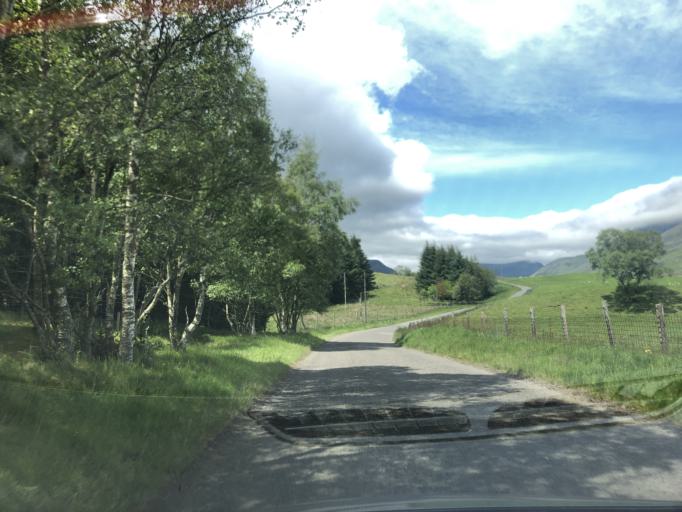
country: GB
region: Scotland
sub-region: Angus
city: Kirriemuir
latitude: 56.8345
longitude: -3.0885
